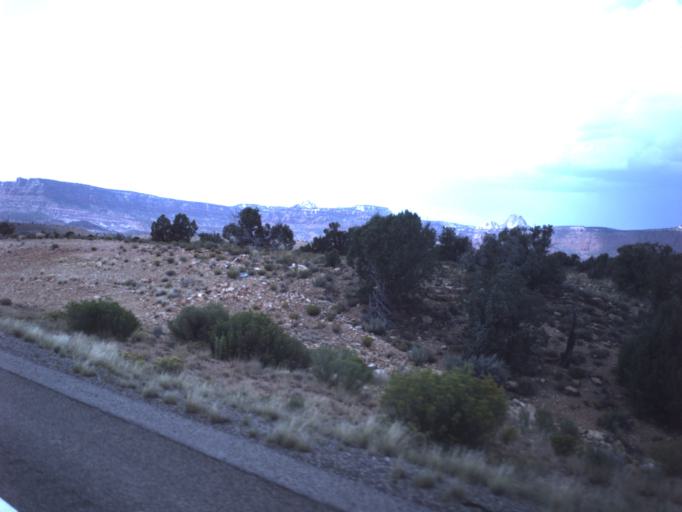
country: US
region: Utah
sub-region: Kane County
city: Kanab
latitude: 37.1862
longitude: -111.9875
